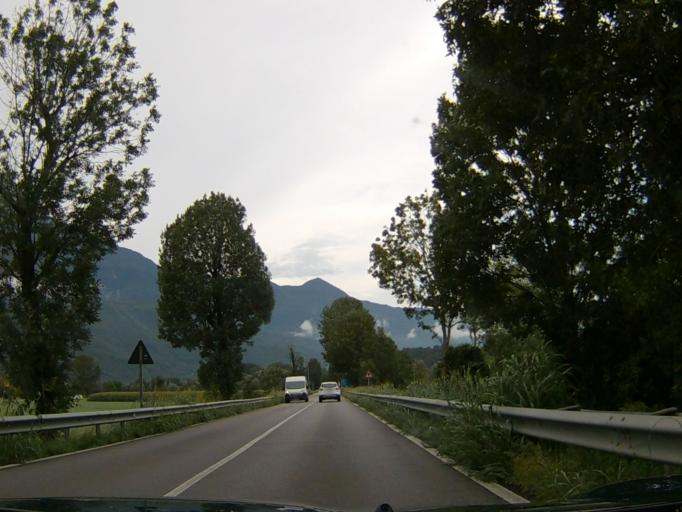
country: IT
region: Lombardy
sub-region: Provincia di Sondrio
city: Dubino
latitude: 46.1602
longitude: 9.4216
